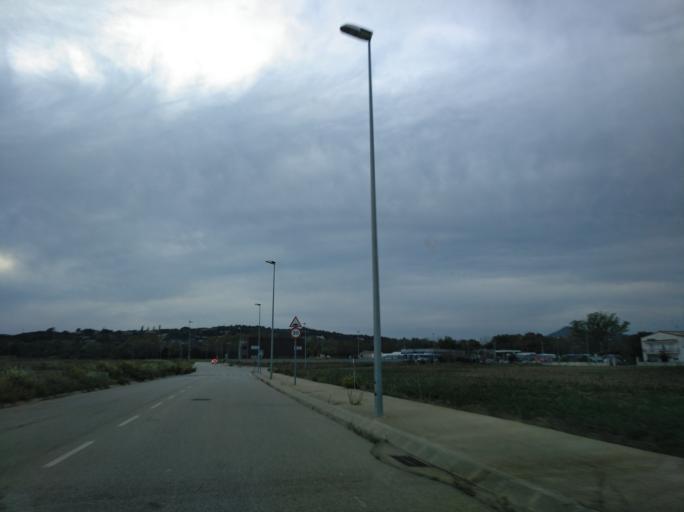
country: ES
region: Catalonia
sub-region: Provincia de Girona
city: Vilablareix
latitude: 41.9624
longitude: 2.7753
